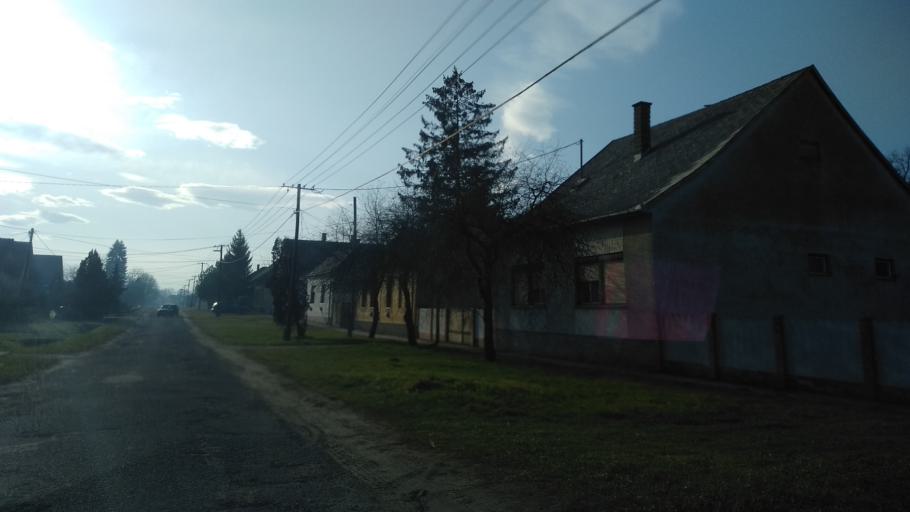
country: HU
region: Somogy
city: Barcs
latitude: 45.9647
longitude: 17.4777
